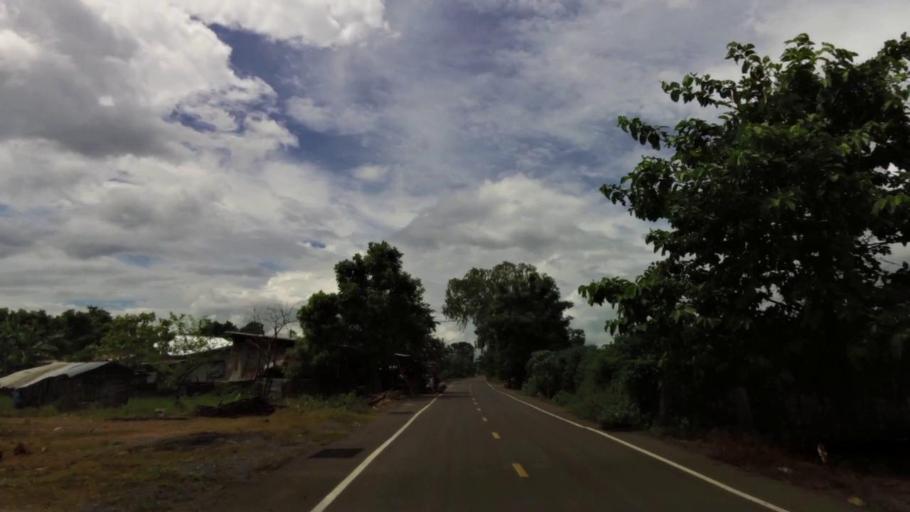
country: TH
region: Nakhon Sawan
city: Phai Sali
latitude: 15.6027
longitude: 100.6542
